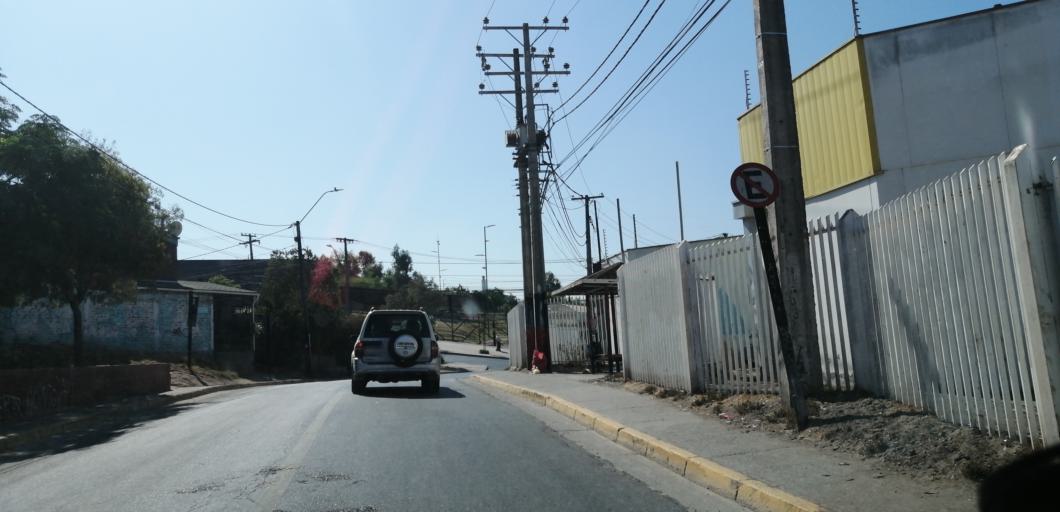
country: CL
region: Santiago Metropolitan
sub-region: Provincia de Santiago
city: Lo Prado
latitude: -33.4474
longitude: -70.7548
